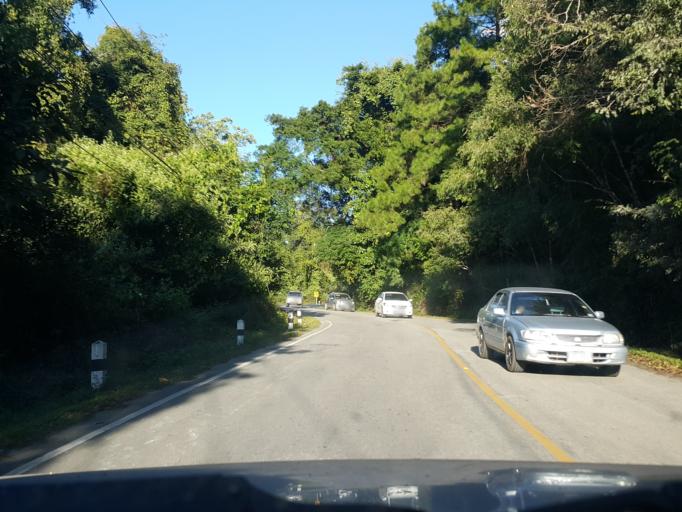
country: TH
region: Mae Hong Son
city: Mae Hi
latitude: 19.2716
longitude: 98.5413
